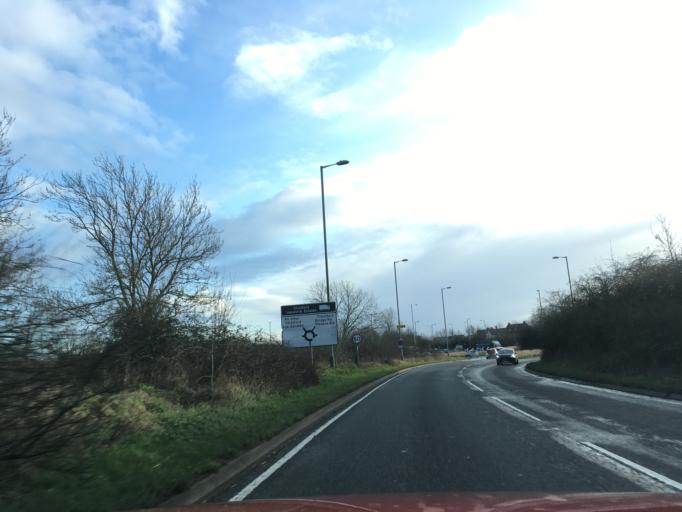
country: GB
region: England
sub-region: Warwickshire
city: Stratford-upon-Avon
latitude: 52.2119
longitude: -1.7257
